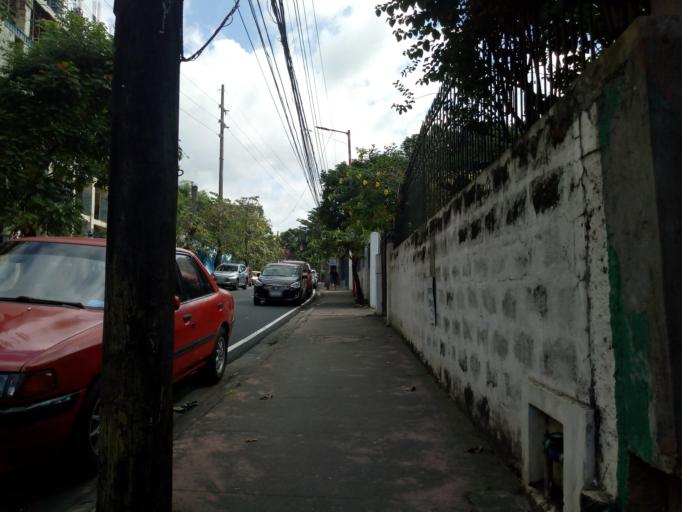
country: PH
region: Calabarzon
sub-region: Province of Rizal
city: Antipolo
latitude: 14.6406
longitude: 121.1178
